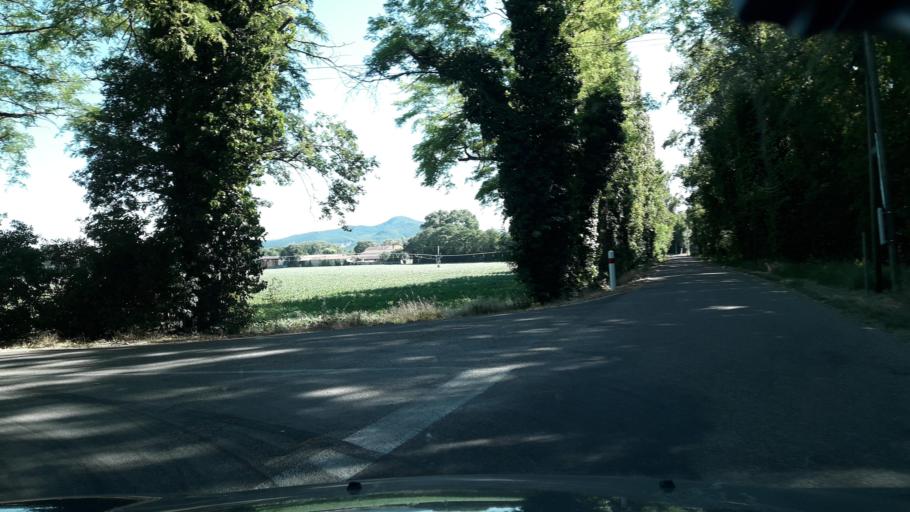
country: FR
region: Rhone-Alpes
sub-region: Departement de l'Ardeche
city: Le Pouzin
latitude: 44.7532
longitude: 4.7658
